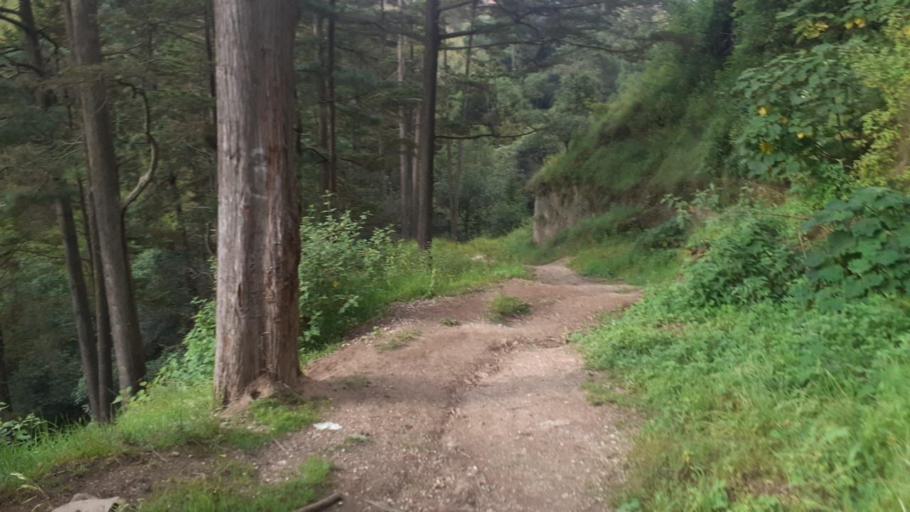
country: GT
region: Quetzaltenango
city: Cantel
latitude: 14.8206
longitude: -91.4470
